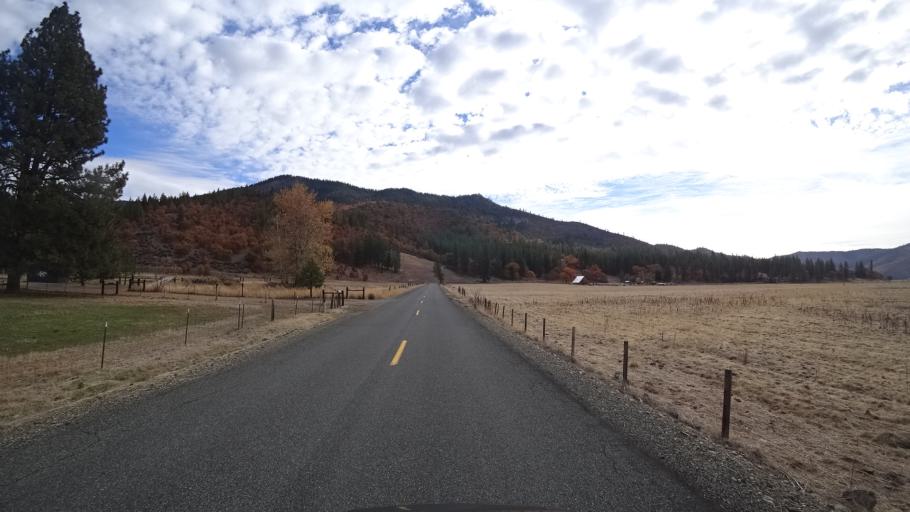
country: US
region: California
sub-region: Siskiyou County
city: Yreka
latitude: 41.6562
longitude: -122.8351
